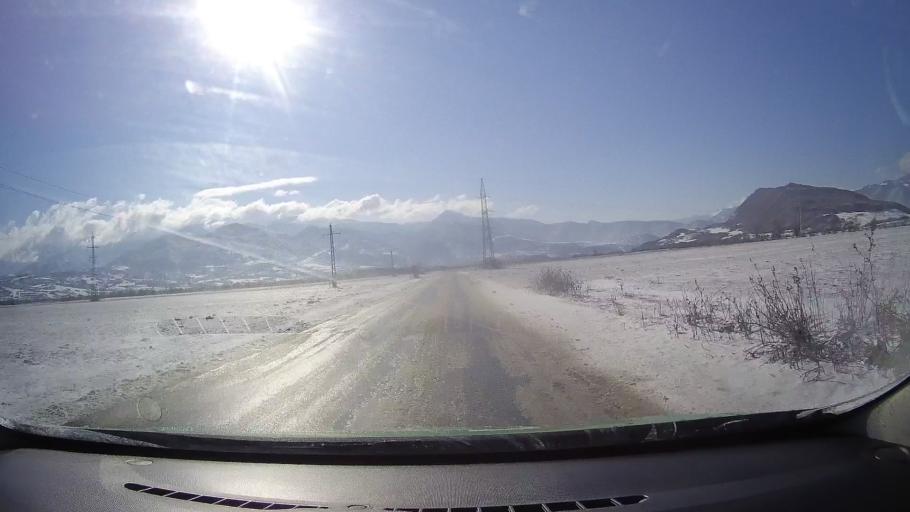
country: RO
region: Sibiu
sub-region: Comuna Turnu Rosu
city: Turnu Rosu
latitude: 45.6607
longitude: 24.2966
